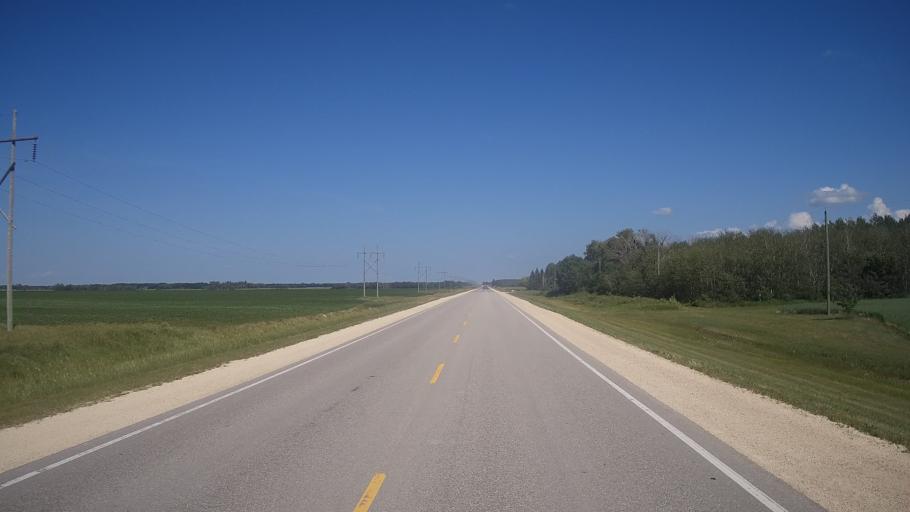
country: CA
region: Manitoba
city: Stonewall
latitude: 50.1227
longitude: -97.3866
